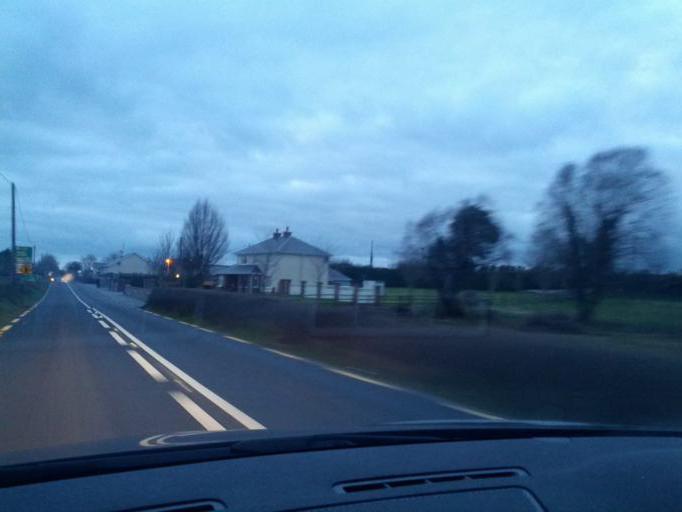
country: IE
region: Connaught
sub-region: County Galway
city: Portumna
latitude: 53.1617
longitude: -8.2791
